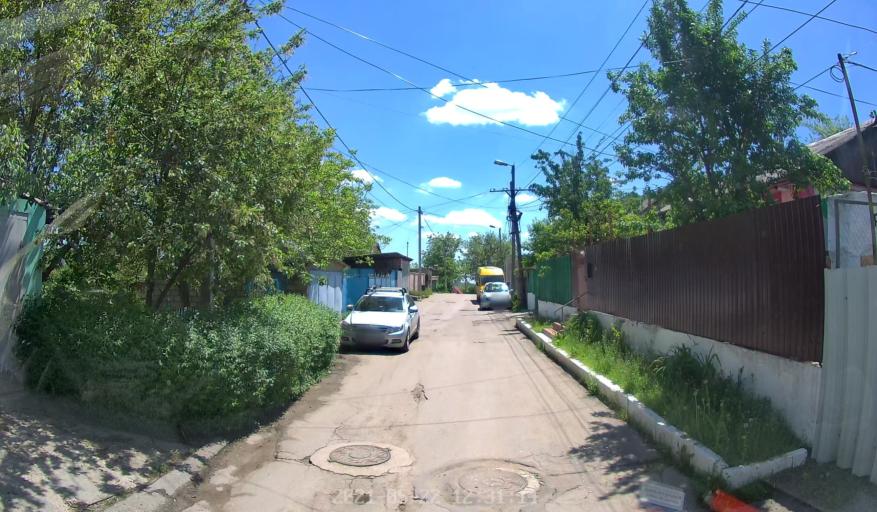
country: MD
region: Chisinau
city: Chisinau
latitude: 47.0521
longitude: 28.8316
